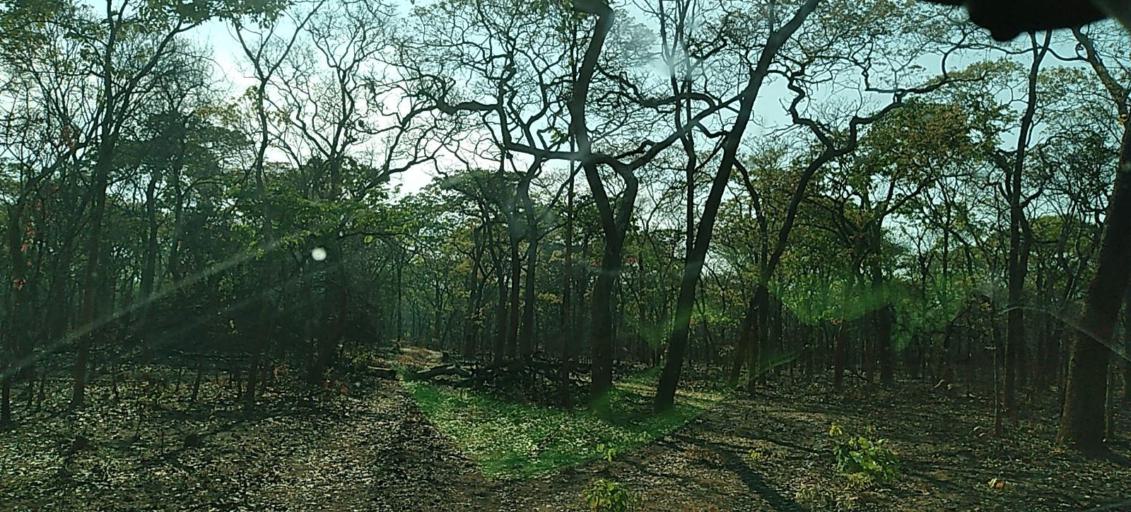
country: ZM
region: North-Western
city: Kalengwa
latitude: -13.2280
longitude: 25.0849
